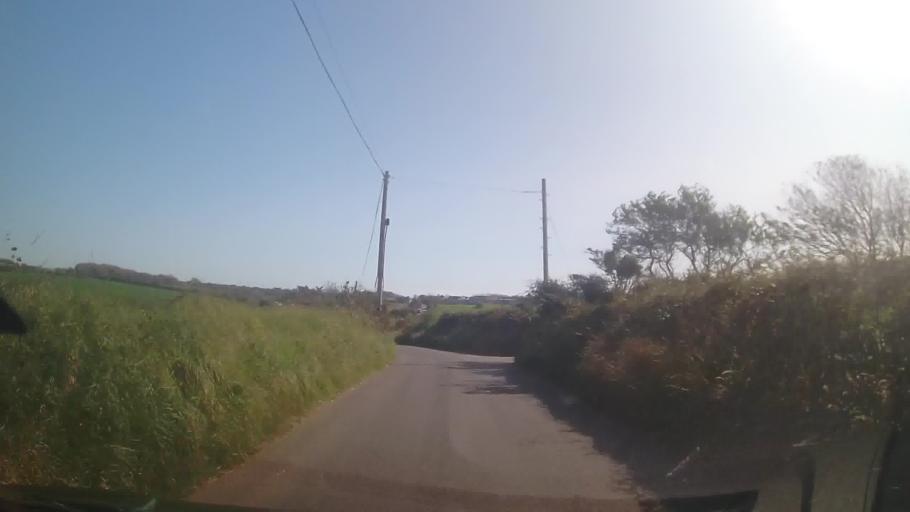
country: GB
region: Wales
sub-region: Pembrokeshire
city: Llanrhian
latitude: 51.9324
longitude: -5.1662
